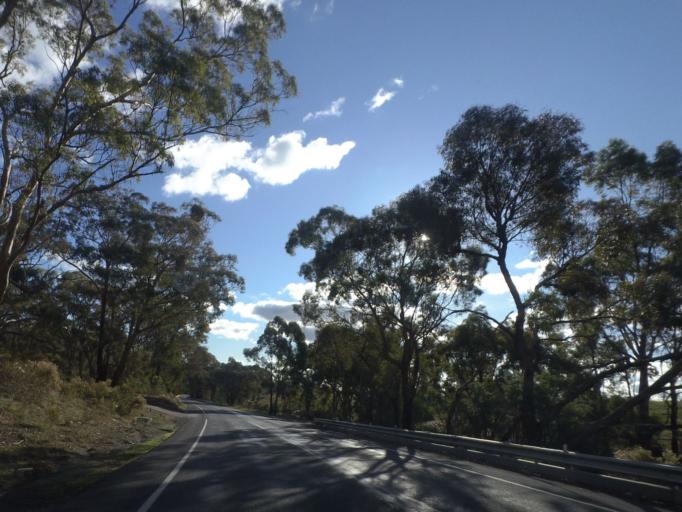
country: AU
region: Victoria
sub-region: Mount Alexander
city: Castlemaine
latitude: -37.1041
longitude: 144.3009
